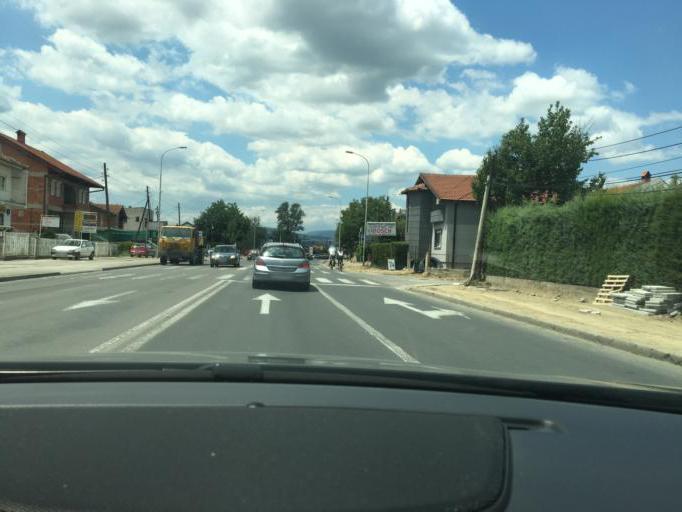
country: MK
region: Saraj
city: Saraj
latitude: 42.0061
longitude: 21.3471
